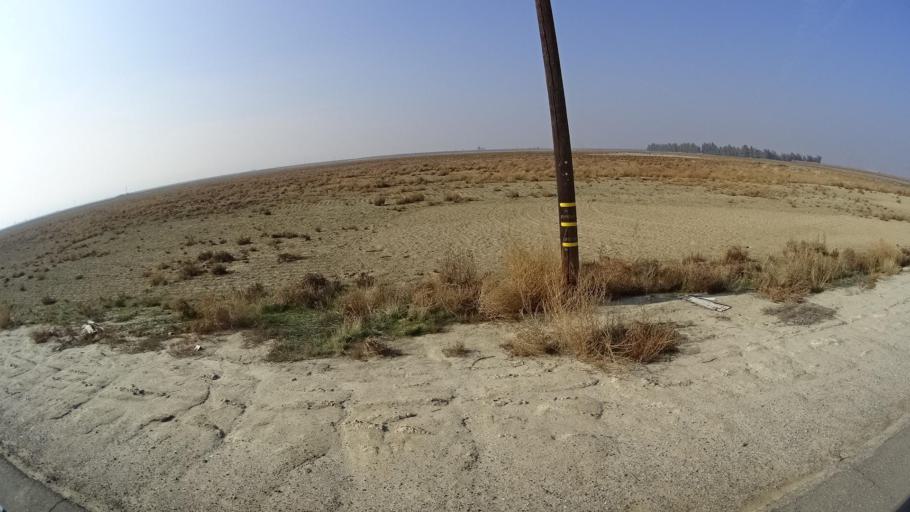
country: US
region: California
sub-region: Kern County
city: Buttonwillow
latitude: 35.3503
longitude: -119.3591
